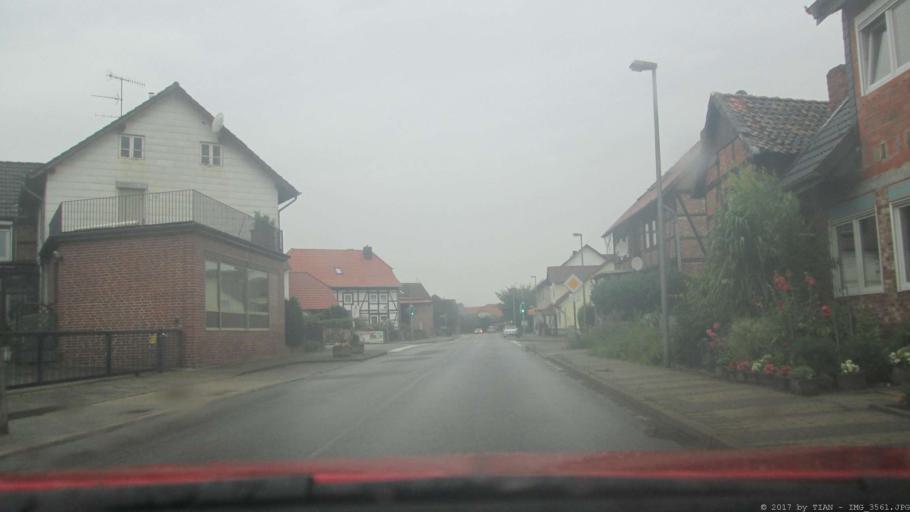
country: DE
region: Lower Saxony
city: Konigslutter am Elm
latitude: 52.3328
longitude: 10.8348
